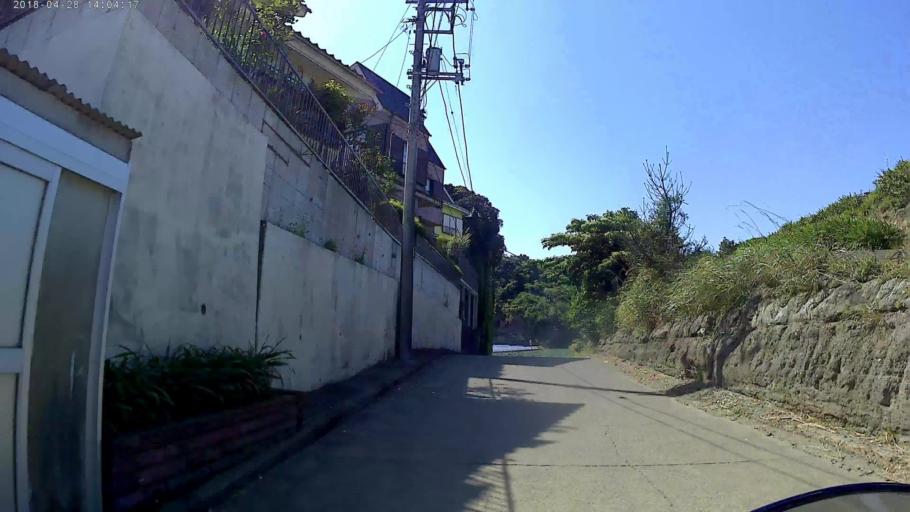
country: JP
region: Kanagawa
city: Miura
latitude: 35.1602
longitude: 139.6560
